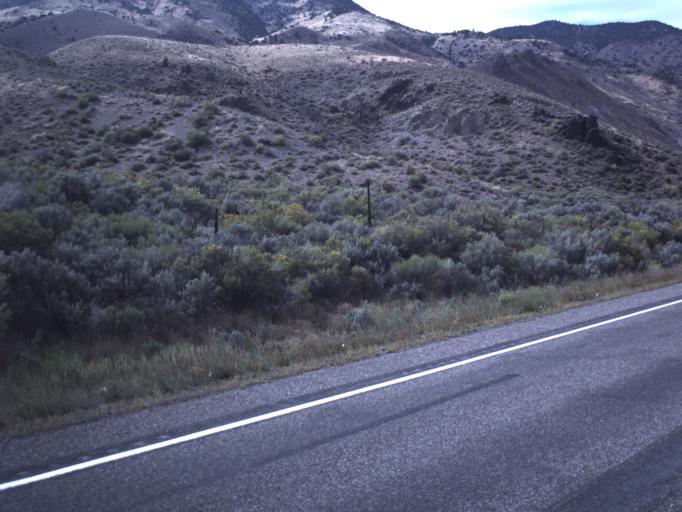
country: US
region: Utah
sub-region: Sevier County
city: Monroe
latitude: 38.4763
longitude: -112.2395
